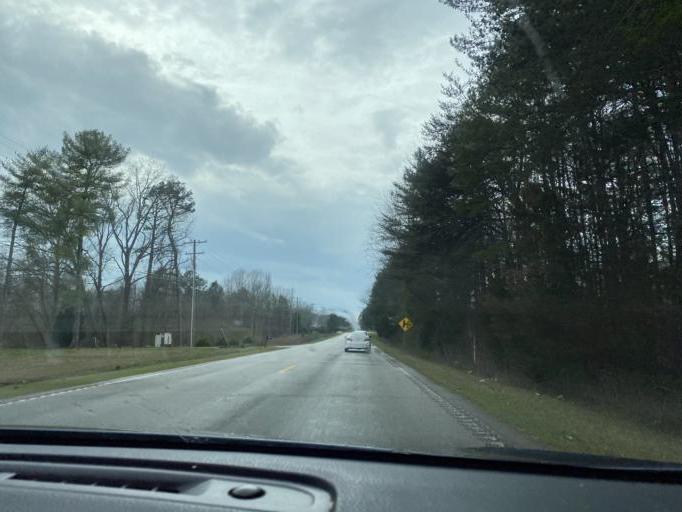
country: US
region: South Carolina
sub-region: Spartanburg County
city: Cowpens
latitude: 35.0167
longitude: -81.7635
